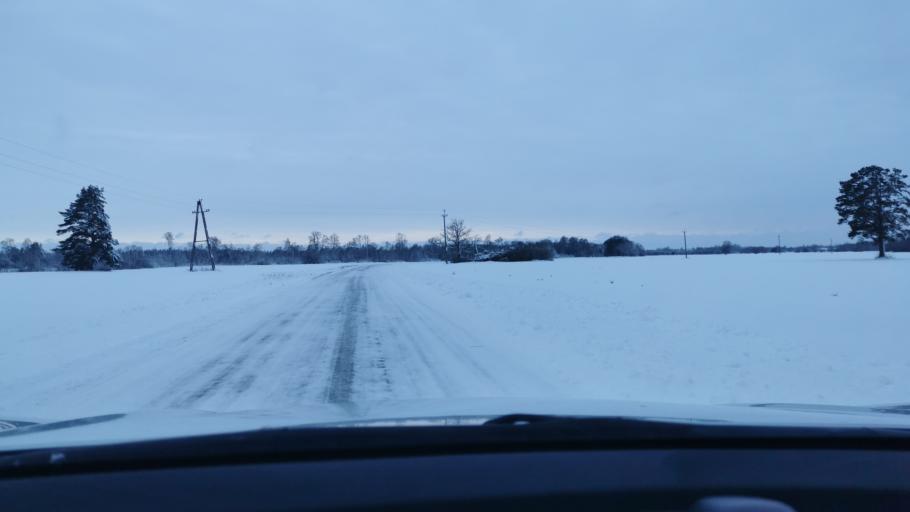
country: EE
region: Laeaene-Virumaa
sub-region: Viru-Nigula vald
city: Kunda
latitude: 59.4547
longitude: 26.5280
